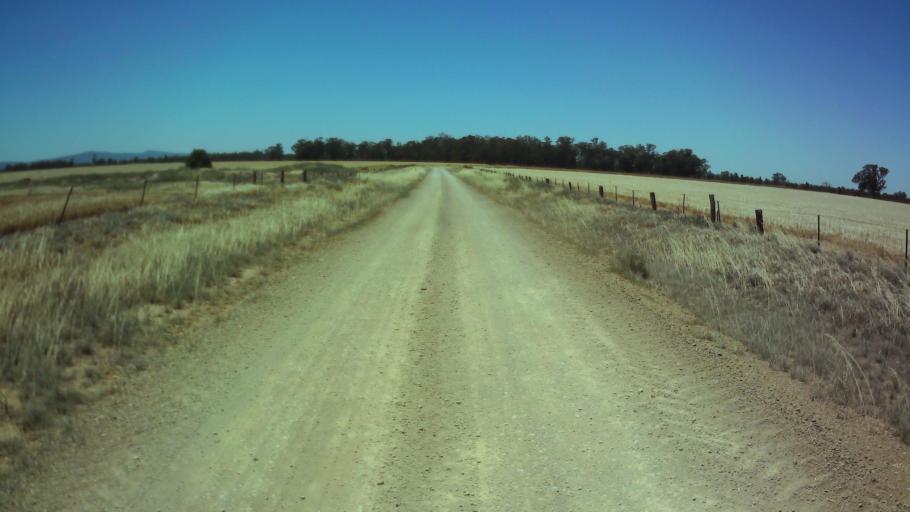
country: AU
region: New South Wales
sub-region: Weddin
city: Grenfell
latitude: -34.0425
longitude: 147.7962
